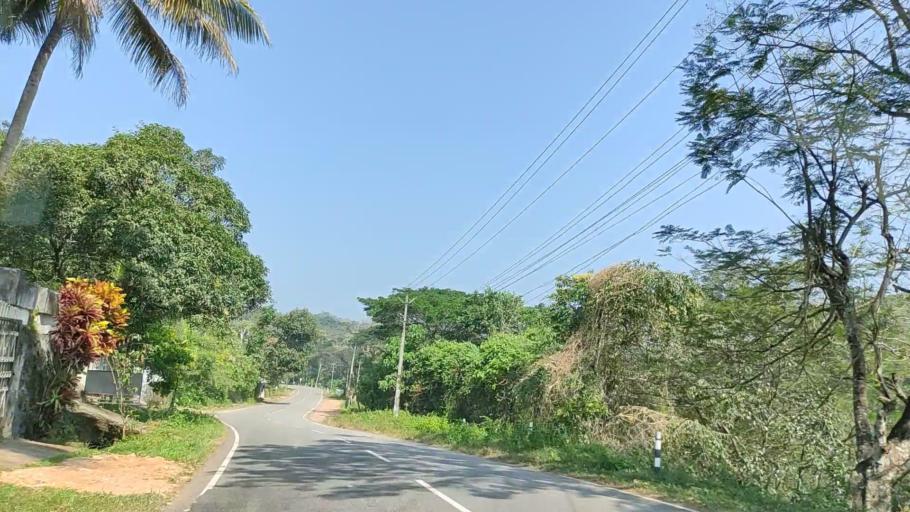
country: IN
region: Kerala
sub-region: Kollam
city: Punalur
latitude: 8.9263
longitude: 77.0648
